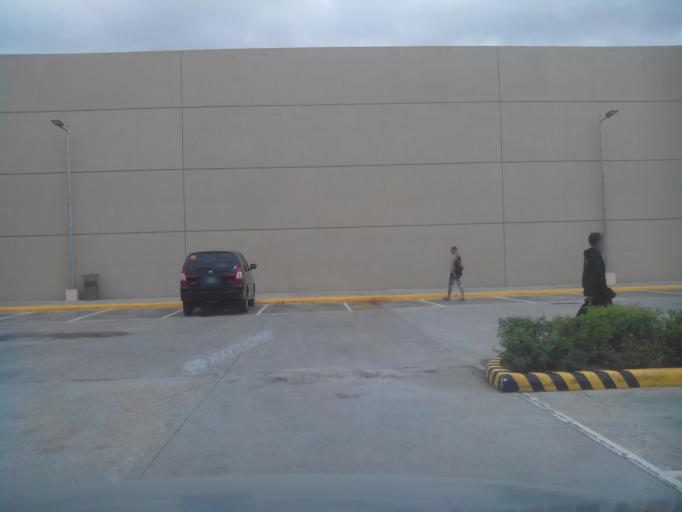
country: PH
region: Calabarzon
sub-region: Province of Rizal
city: Cainta
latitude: 14.5958
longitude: 121.1738
